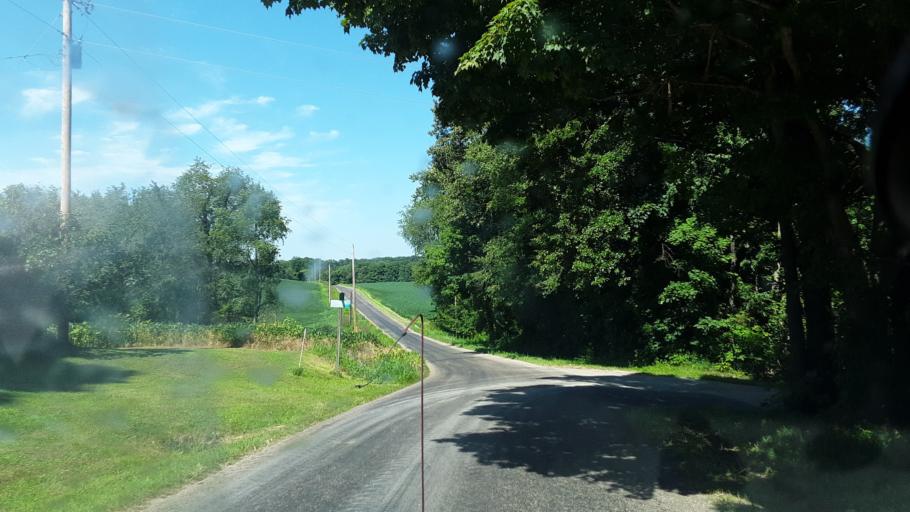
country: US
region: Ohio
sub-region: Knox County
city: Gambier
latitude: 40.3791
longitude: -82.3293
